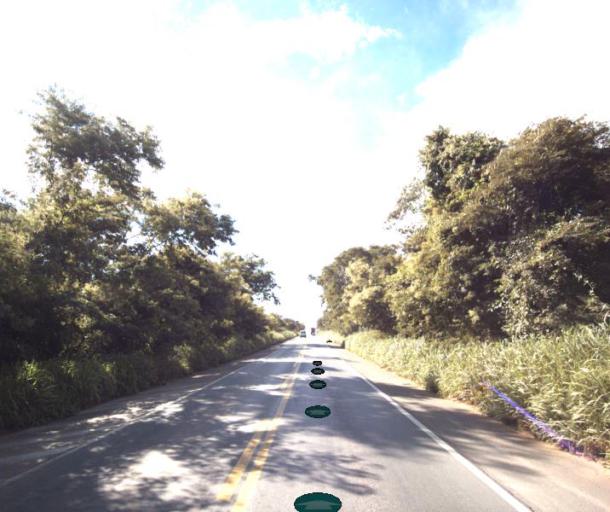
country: BR
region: Goias
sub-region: Jaragua
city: Jaragua
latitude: -15.5702
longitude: -49.4197
